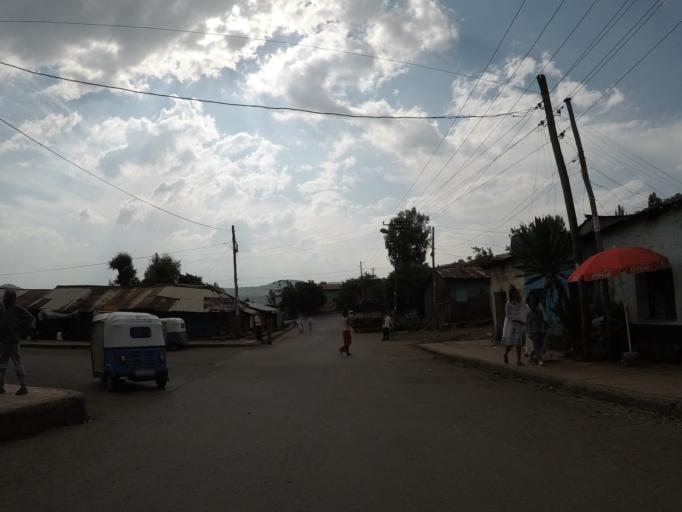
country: ET
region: Amhara
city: Gondar
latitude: 12.6153
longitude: 37.4703
